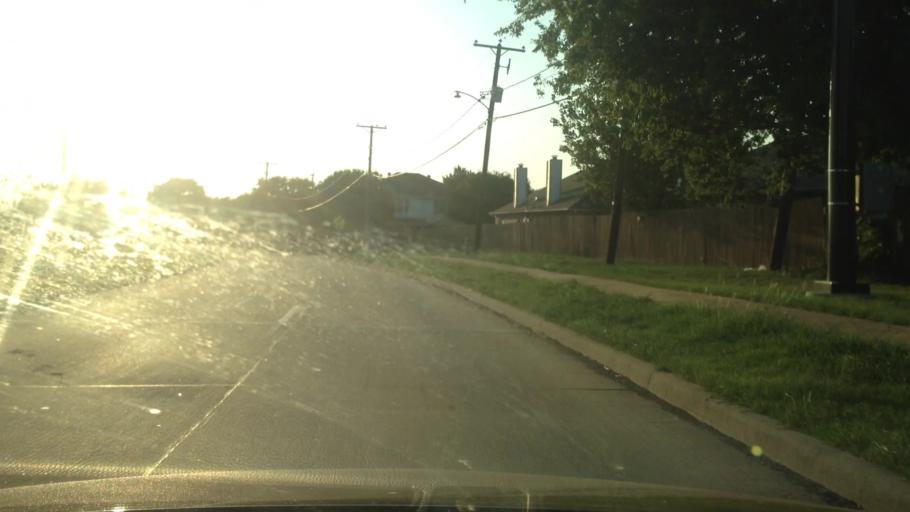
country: US
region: Texas
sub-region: Tarrant County
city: Dalworthington Gardens
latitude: 32.6484
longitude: -97.1275
